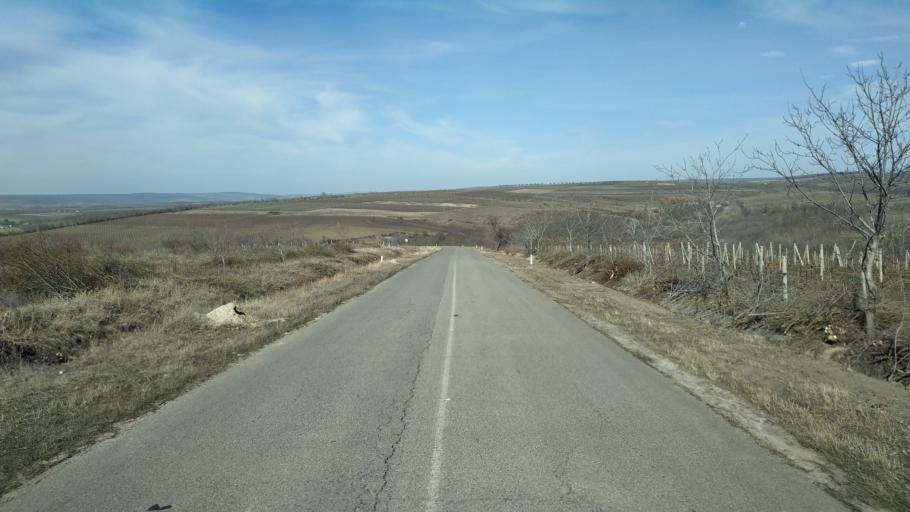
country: MD
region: Nisporeni
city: Nisporeni
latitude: 46.9548
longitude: 28.2365
